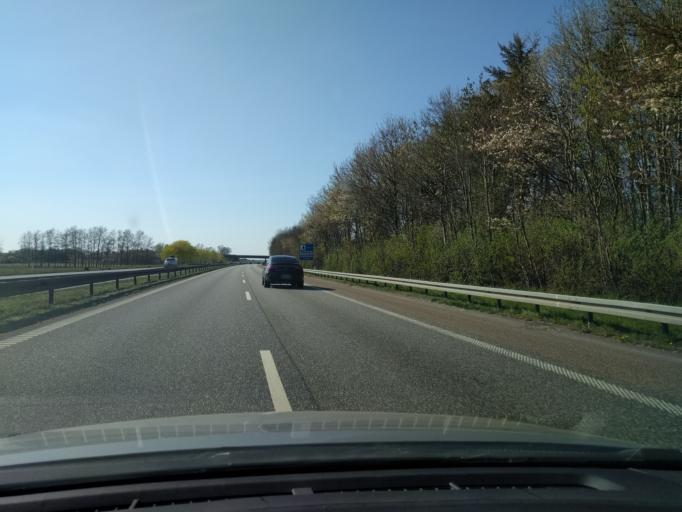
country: DK
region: Zealand
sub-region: Soro Kommune
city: Frederiksberg
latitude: 55.4499
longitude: 11.6304
